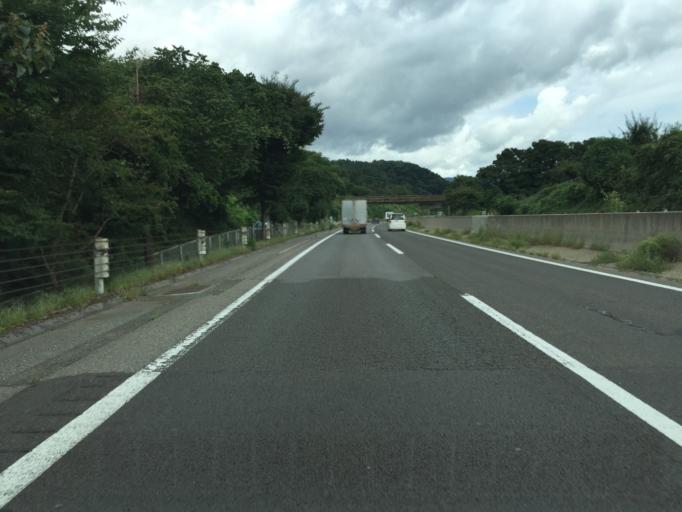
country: JP
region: Fukushima
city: Hobaramachi
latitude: 37.8468
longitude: 140.5061
